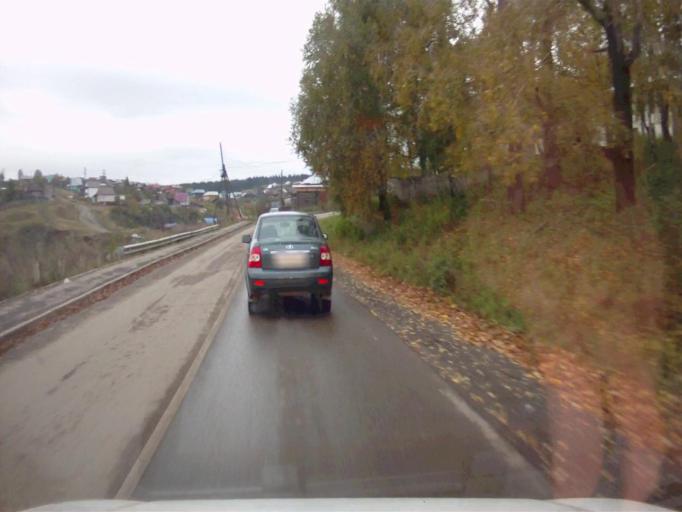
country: RU
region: Chelyabinsk
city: Nyazepetrovsk
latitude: 56.0570
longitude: 59.5890
